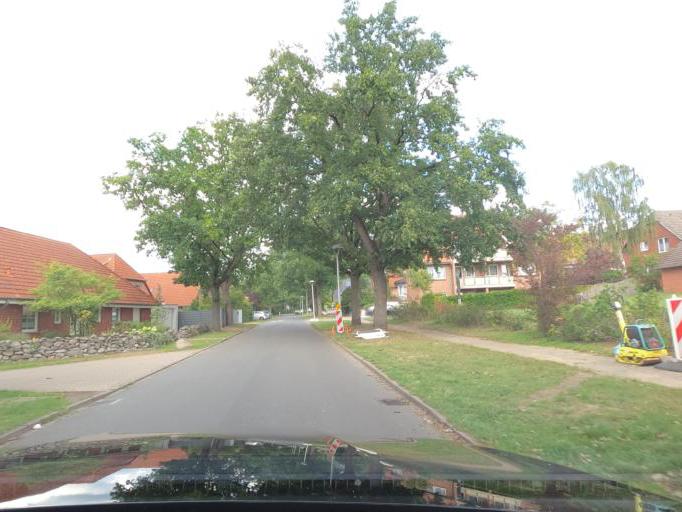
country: DE
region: Lower Saxony
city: Isernhagen Farster Bauerschaft
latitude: 52.5159
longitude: 9.9211
